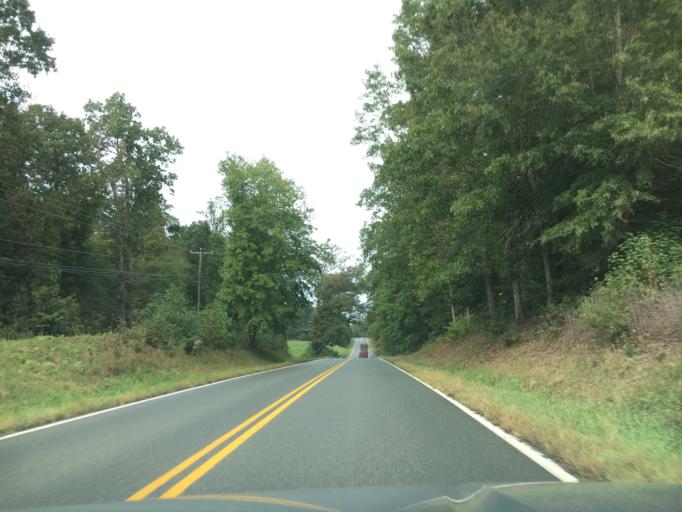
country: US
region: Virginia
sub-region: Goochland County
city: Goochland
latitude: 37.7367
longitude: -77.8418
